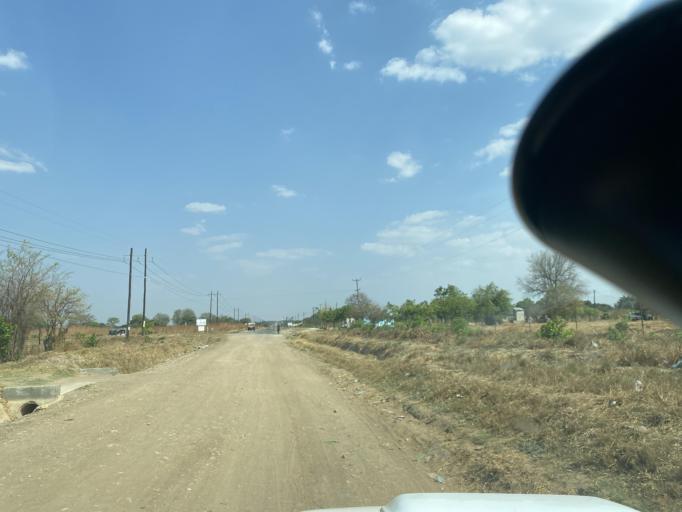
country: ZM
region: Lusaka
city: Lusaka
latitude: -15.3175
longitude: 28.0609
